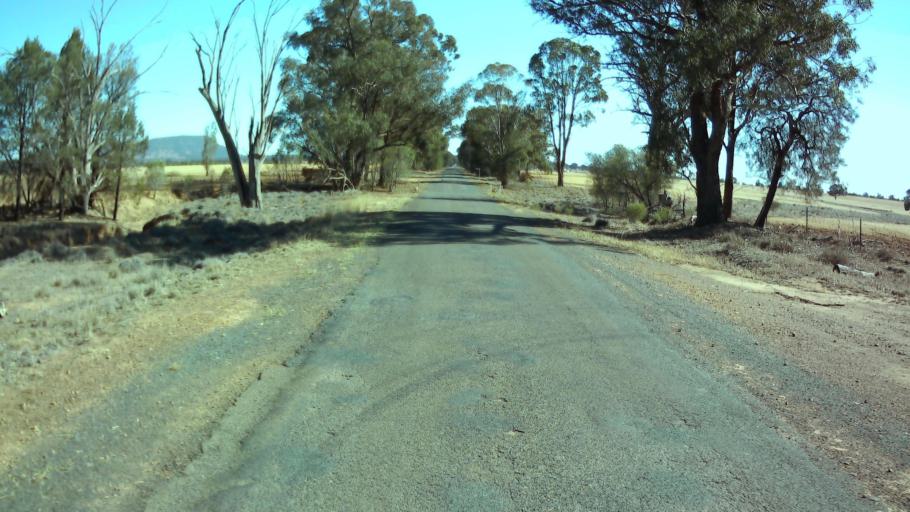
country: AU
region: New South Wales
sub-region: Weddin
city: Grenfell
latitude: -33.8069
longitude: 147.9547
